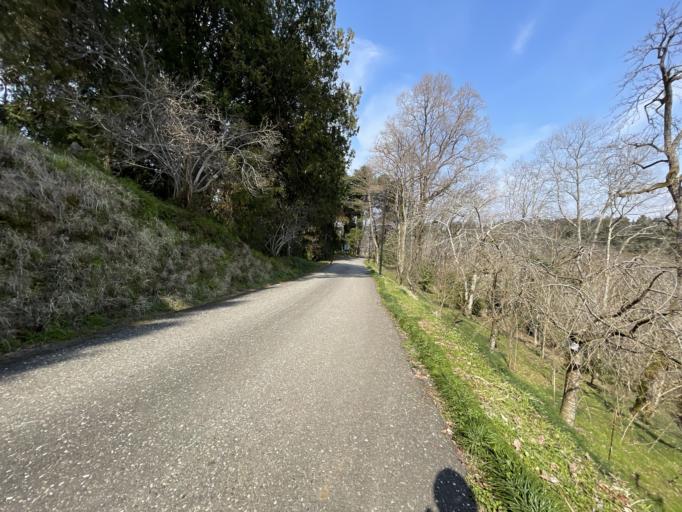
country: GE
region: Ajaria
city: Makhinjauri
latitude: 41.7033
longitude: 41.7216
